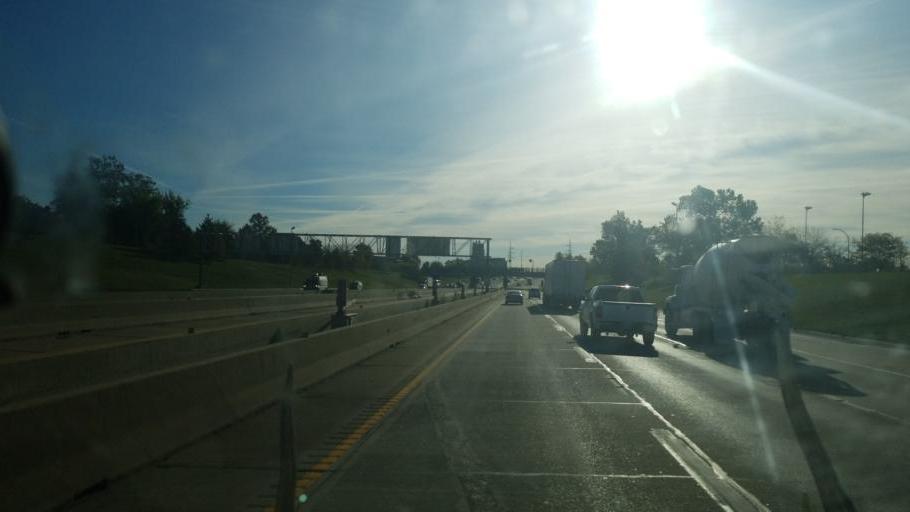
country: US
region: Missouri
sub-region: Saint Louis County
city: Pine Lawn
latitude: 38.6875
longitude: -90.2489
